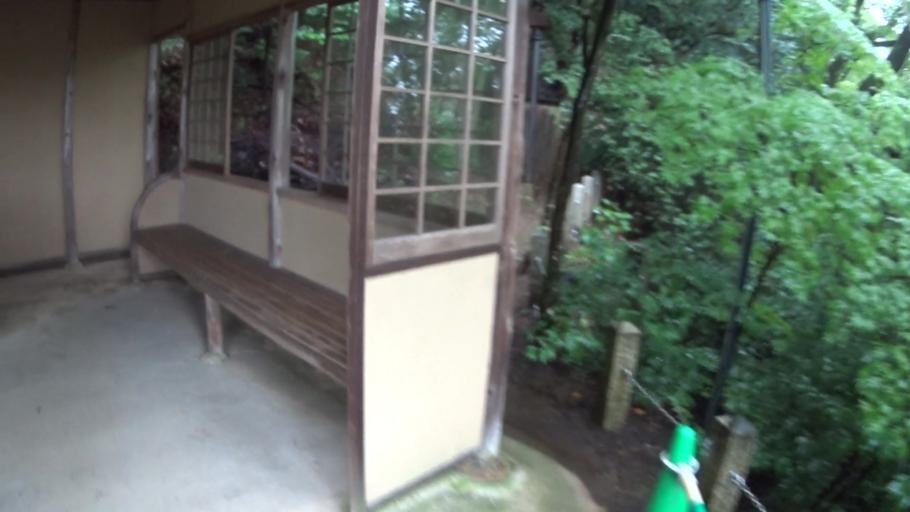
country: JP
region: Kyoto
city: Kyoto
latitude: 35.0080
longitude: 135.7980
